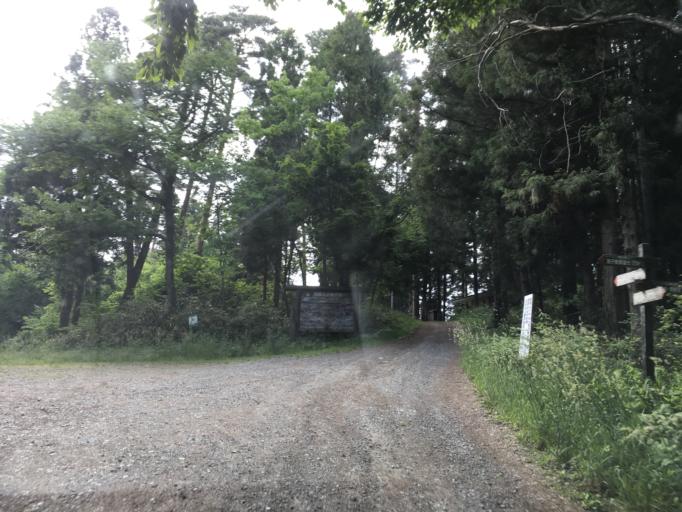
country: JP
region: Iwate
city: Hanamaki
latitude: 39.4009
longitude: 141.1620
